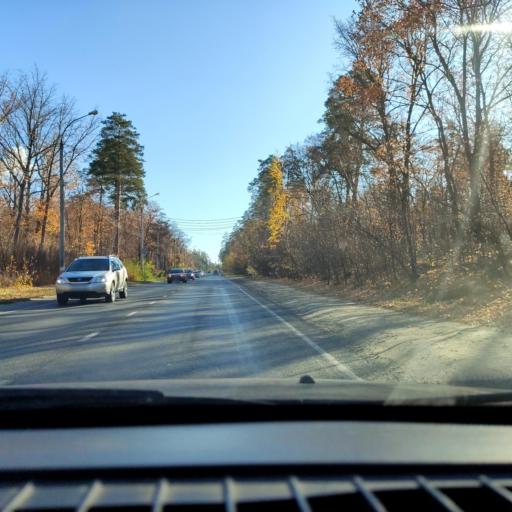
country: RU
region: Samara
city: Tol'yatti
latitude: 53.4936
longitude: 49.2951
